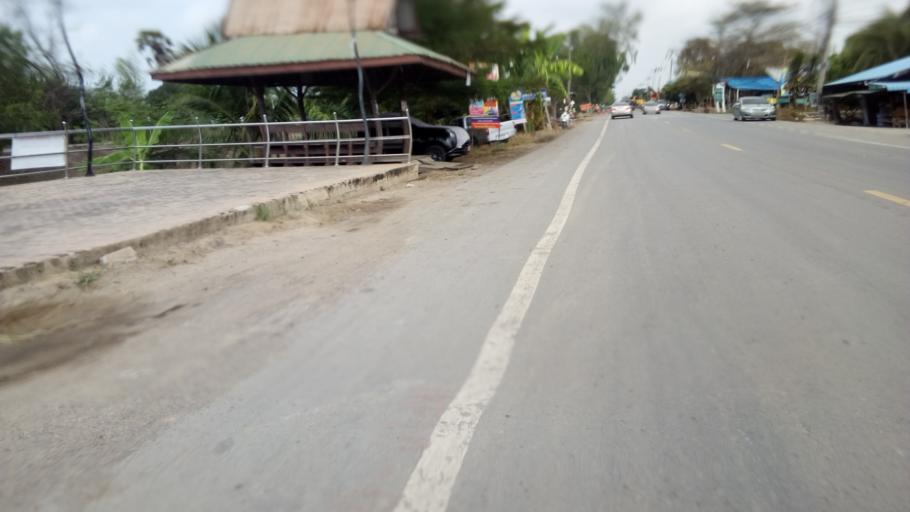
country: TH
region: Pathum Thani
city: Nong Suea
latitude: 14.1971
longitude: 100.8235
